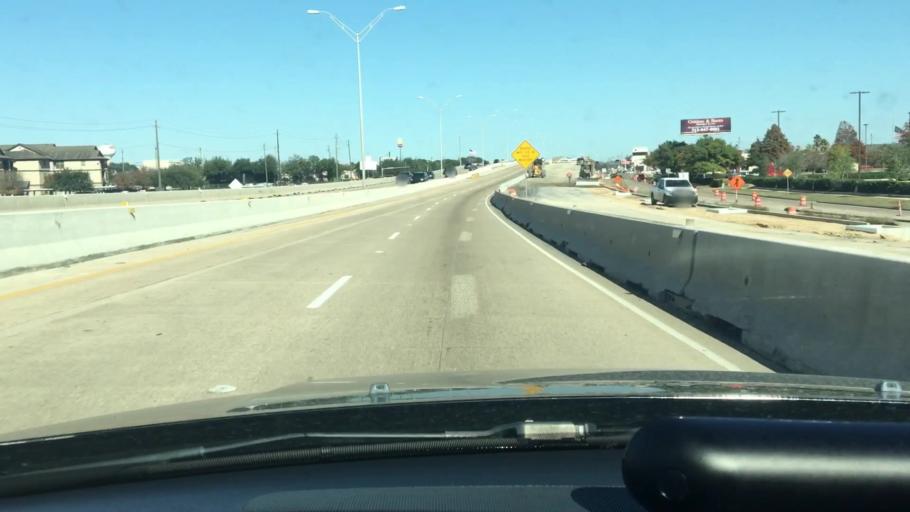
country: US
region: Texas
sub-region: Harris County
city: Deer Park
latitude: 29.6789
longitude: -95.1560
